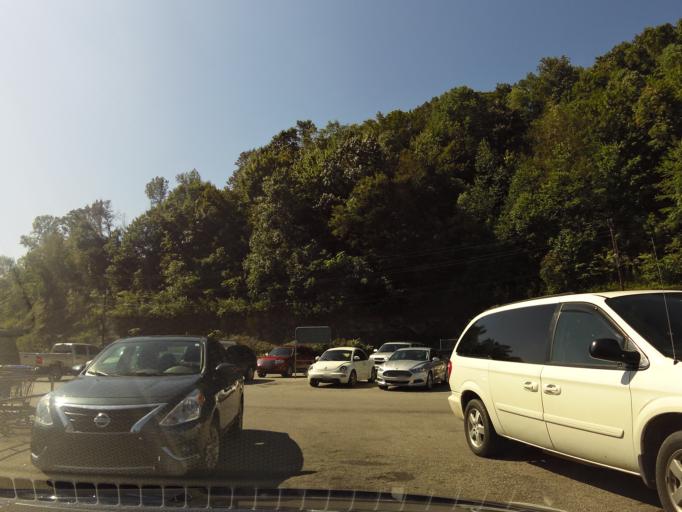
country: US
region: Kentucky
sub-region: Clay County
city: Manchester
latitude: 37.1405
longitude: -83.7724
